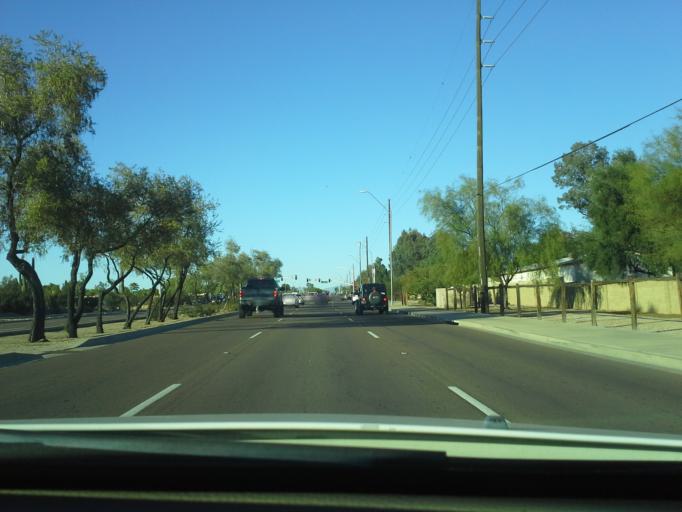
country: US
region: Arizona
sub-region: Maricopa County
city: Paradise Valley
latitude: 33.5946
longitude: -111.9259
